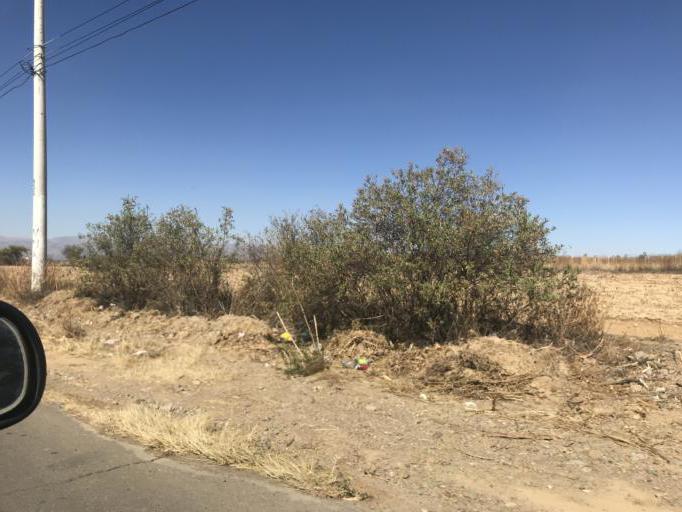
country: BO
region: Cochabamba
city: Tarata
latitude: -17.6040
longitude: -65.9897
